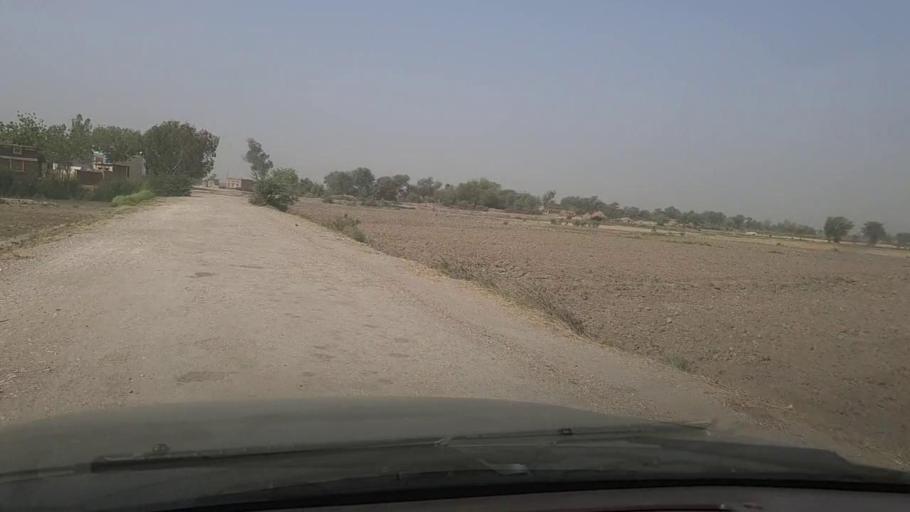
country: PK
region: Sindh
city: Garhi Yasin
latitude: 27.8975
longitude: 68.5877
